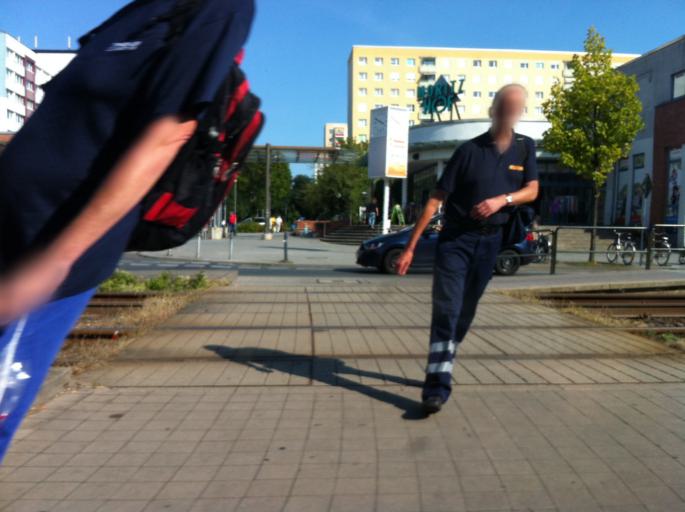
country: DE
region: Saxony
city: Markkleeberg
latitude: 51.3013
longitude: 12.3962
